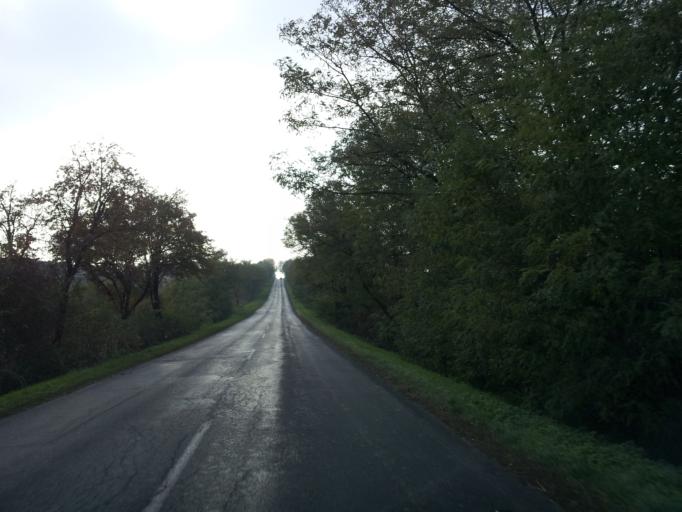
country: HU
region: Komarom-Esztergom
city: Bokod
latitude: 47.5037
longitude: 18.1963
